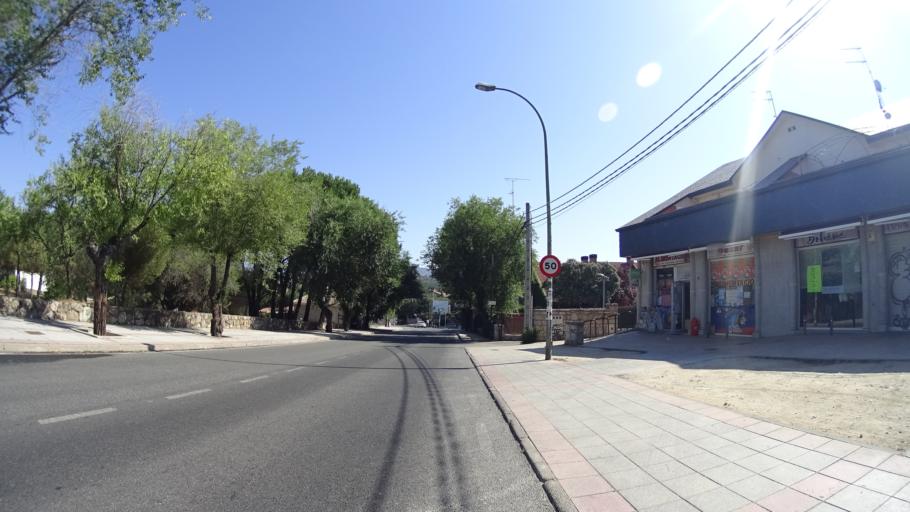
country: ES
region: Madrid
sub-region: Provincia de Madrid
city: Galapagar
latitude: 40.5969
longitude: -3.9844
